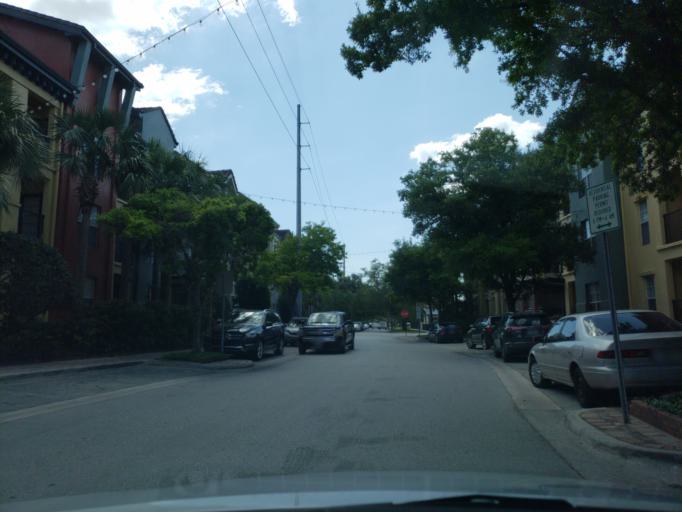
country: US
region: Florida
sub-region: Hillsborough County
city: Tampa
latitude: 27.9398
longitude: -82.4843
